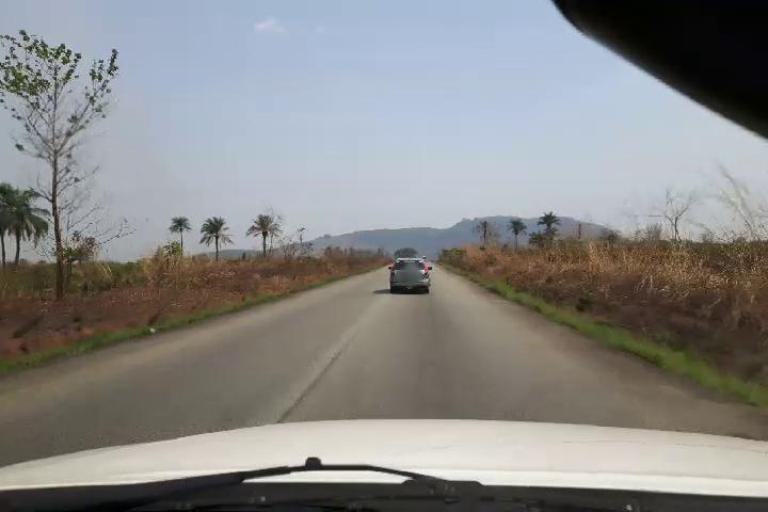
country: SL
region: Northern Province
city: Yonibana
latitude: 8.3917
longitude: -12.1921
